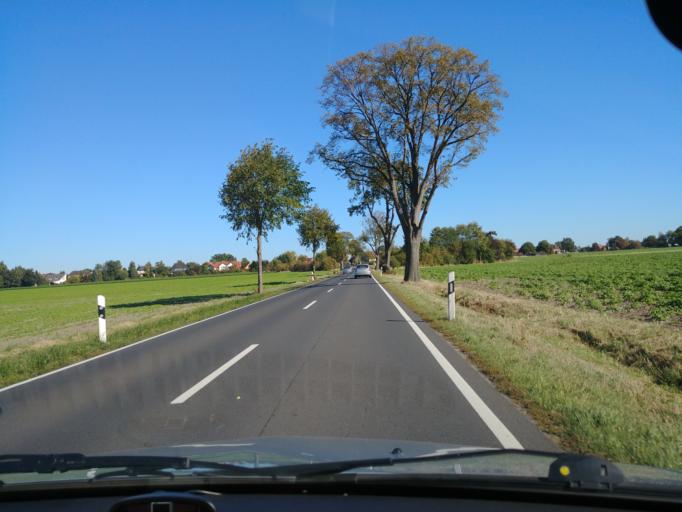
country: DE
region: Lower Saxony
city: Leiferde
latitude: 52.4305
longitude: 10.4319
